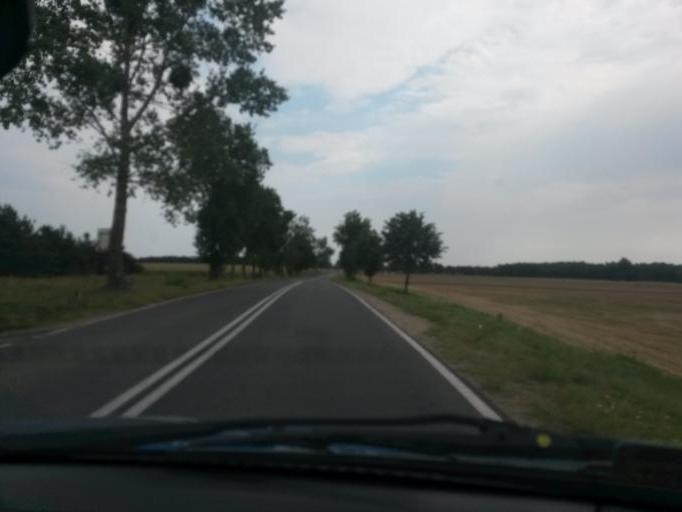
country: PL
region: Masovian Voivodeship
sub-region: Powiat zurominski
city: Lubowidz
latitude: 53.0931
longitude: 19.8630
